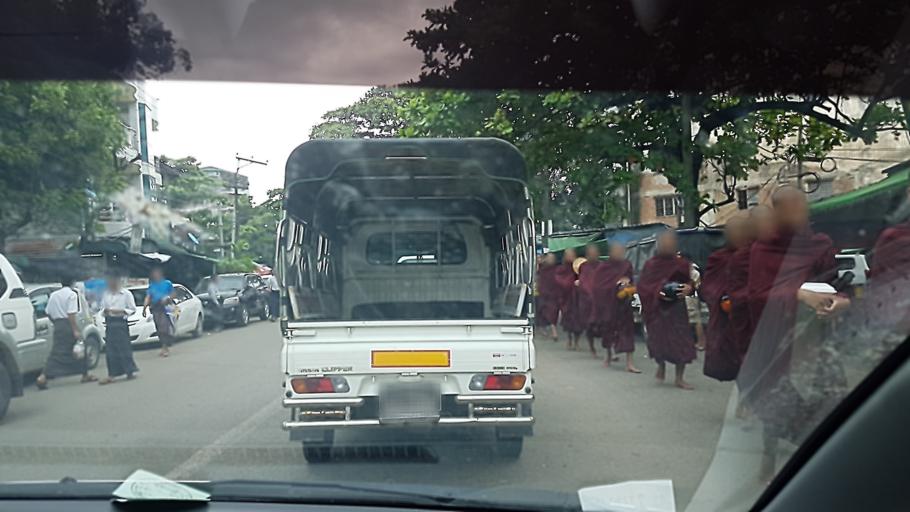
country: MM
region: Yangon
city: Yangon
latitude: 16.8094
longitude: 96.1296
